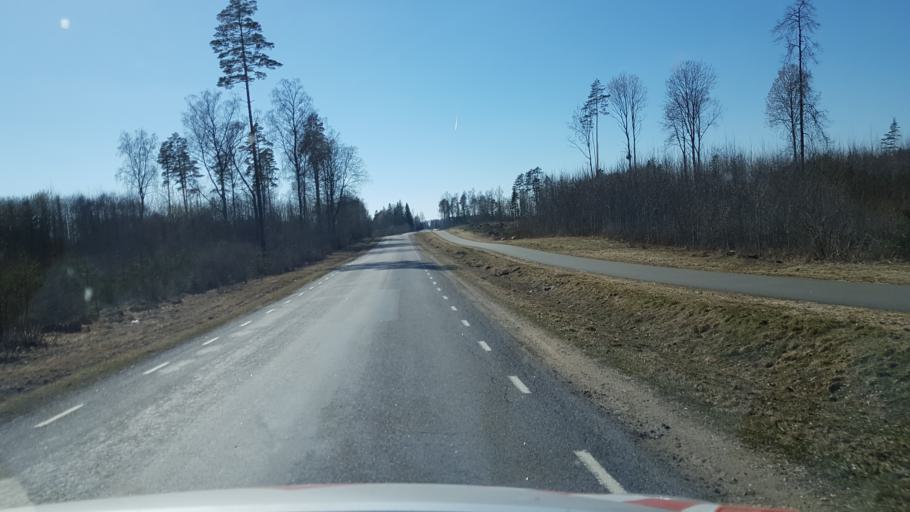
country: EE
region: Laeaene-Virumaa
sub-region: Vaeike-Maarja vald
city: Vaike-Maarja
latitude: 59.0957
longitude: 26.2182
